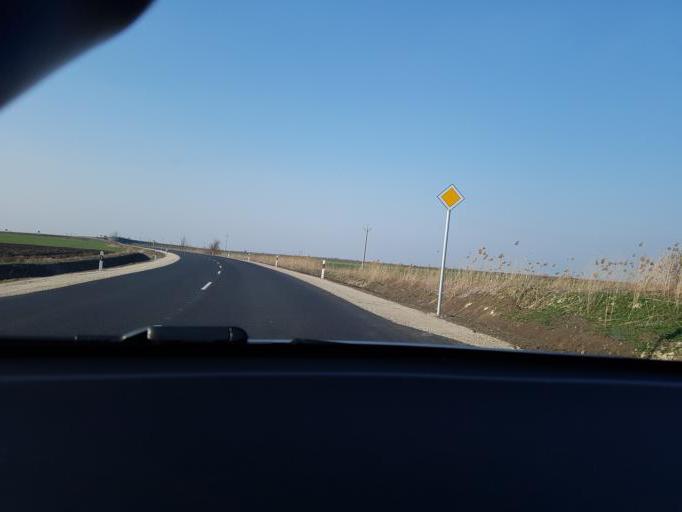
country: HU
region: Csongrad
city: Csanadpalota
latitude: 46.2082
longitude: 20.7185
